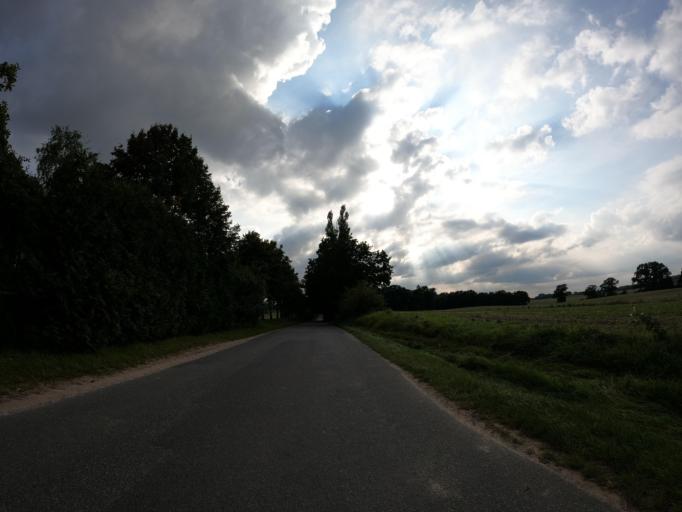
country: DE
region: Mecklenburg-Vorpommern
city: Robel
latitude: 53.4347
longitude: 12.5421
